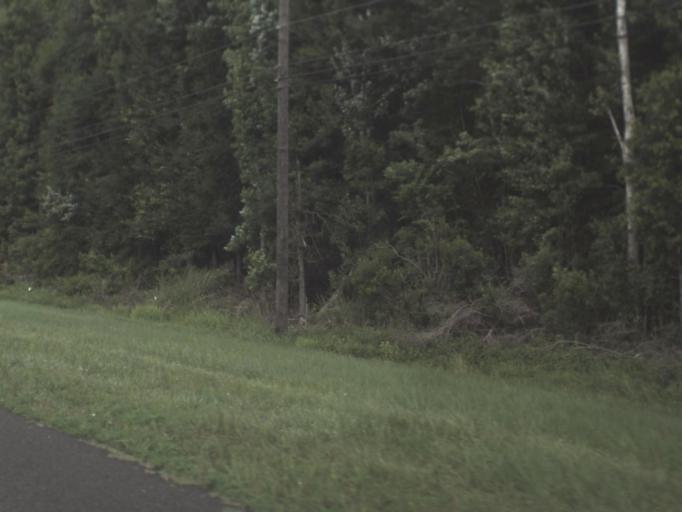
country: US
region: Florida
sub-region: Nassau County
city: Yulee
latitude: 30.6248
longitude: -81.6312
